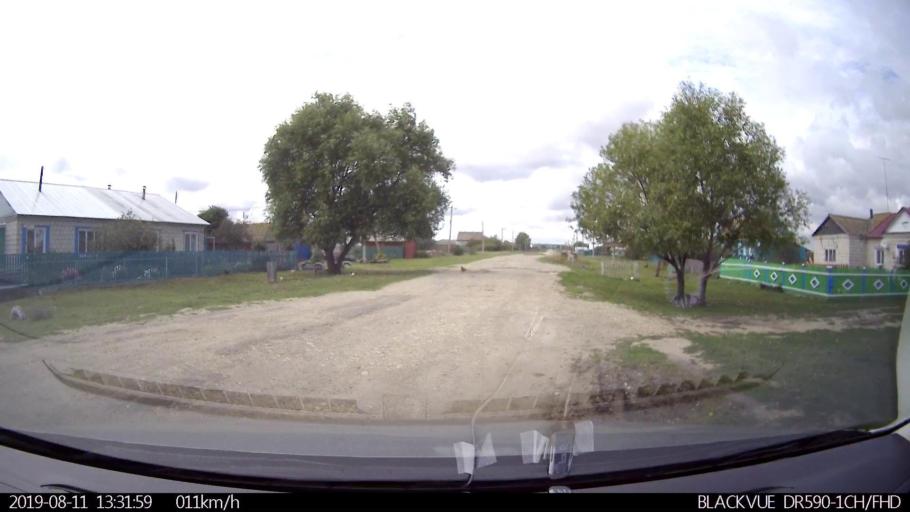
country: RU
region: Ulyanovsk
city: Ignatovka
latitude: 53.8587
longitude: 47.6006
